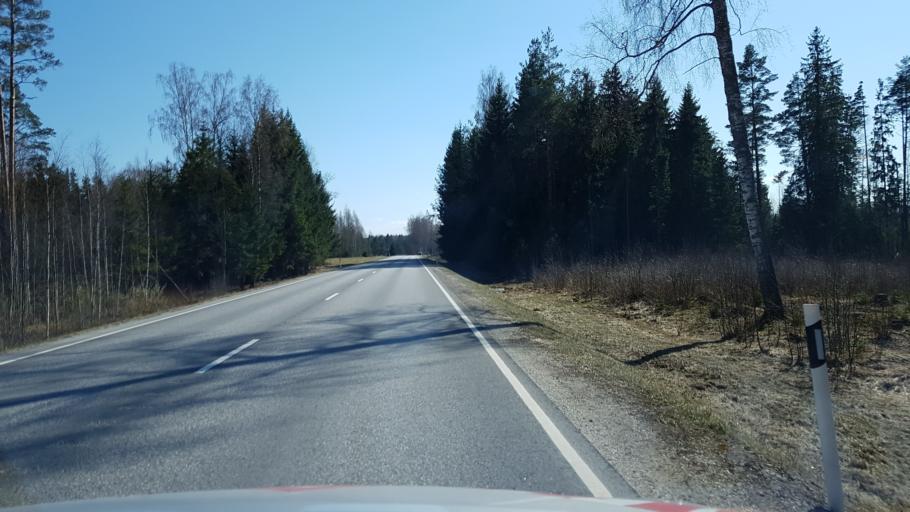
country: EE
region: Jogevamaa
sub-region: Mustvee linn
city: Mustvee
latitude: 58.7026
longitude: 26.8175
